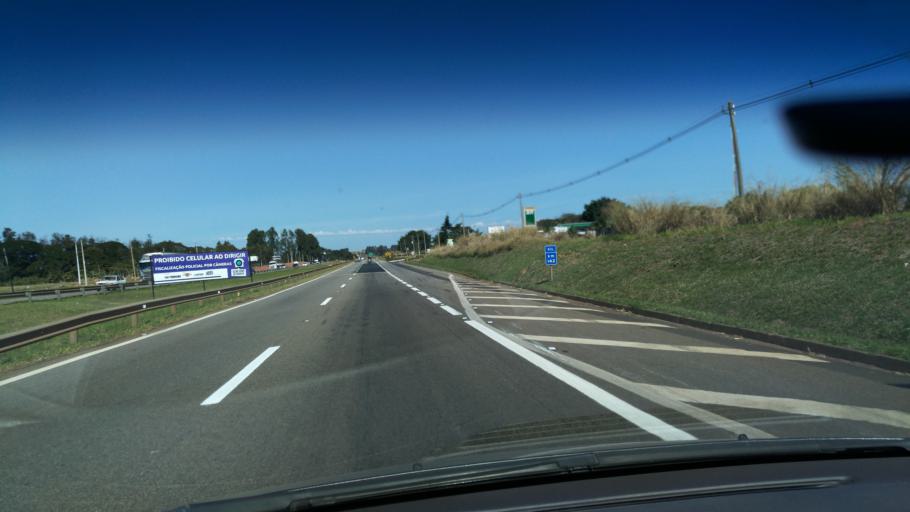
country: BR
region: Sao Paulo
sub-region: Santo Antonio De Posse
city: Santo Antonio de Posse
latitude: -22.6073
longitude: -47.0076
